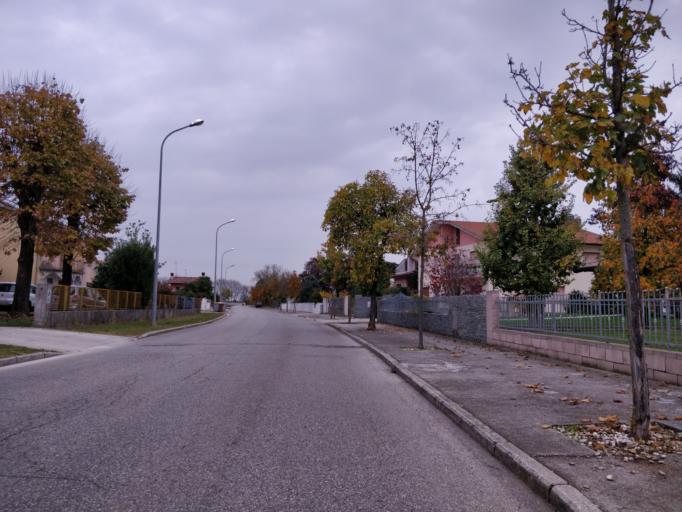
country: IT
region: Friuli Venezia Giulia
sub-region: Provincia di Udine
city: Talmassons
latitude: 45.9307
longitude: 13.1205
